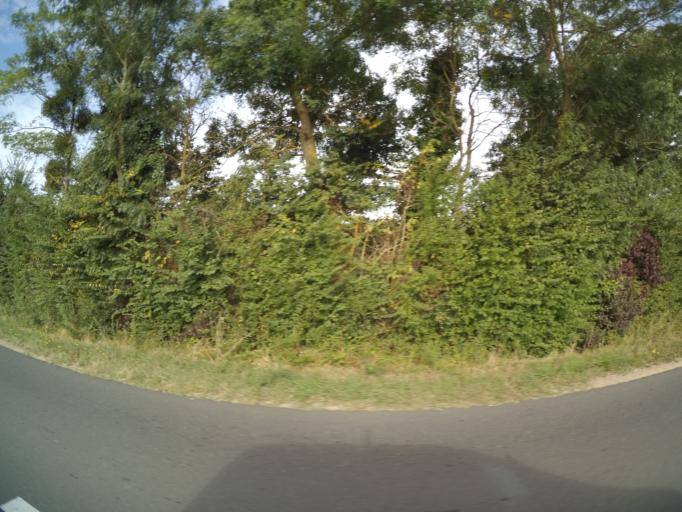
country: FR
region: Pays de la Loire
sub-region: Departement de Maine-et-Loire
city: Martigne-Briand
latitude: 47.2017
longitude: -0.4131
